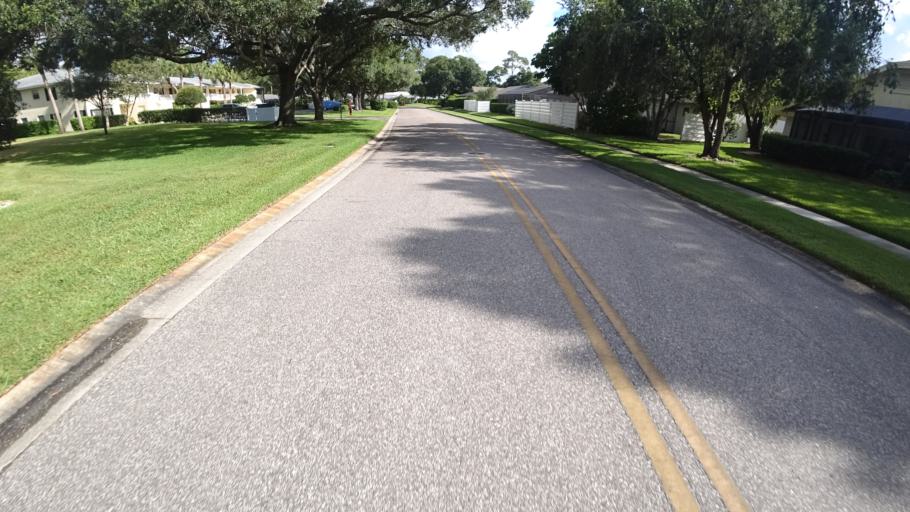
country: US
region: Florida
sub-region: Sarasota County
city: Desoto Lakes
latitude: 27.4004
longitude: -82.4885
